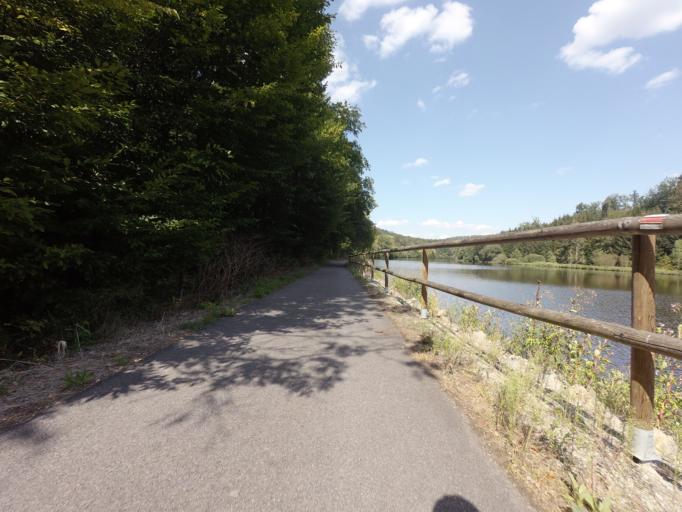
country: CZ
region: Jihocesky
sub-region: Okres Ceske Budejovice
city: Hluboka nad Vltavou
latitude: 49.0780
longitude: 14.4544
